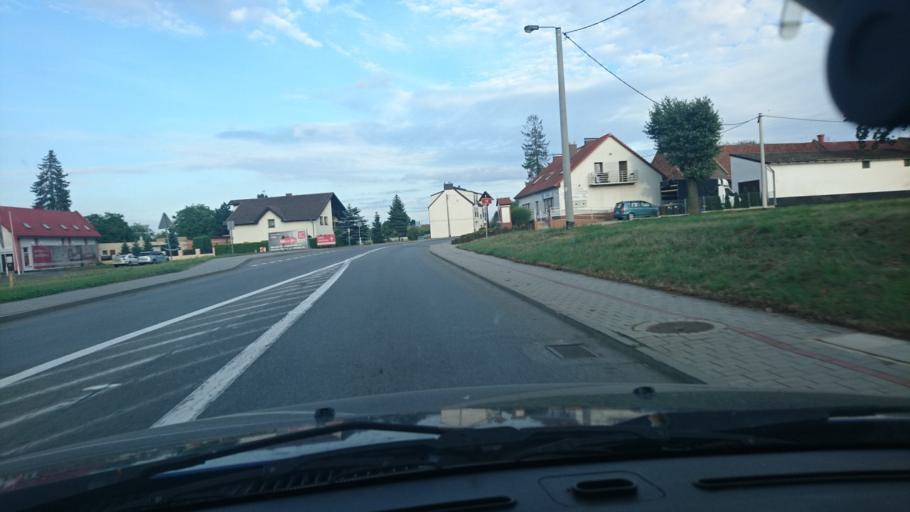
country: PL
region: Opole Voivodeship
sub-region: Powiat oleski
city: Olesno
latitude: 50.8738
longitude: 18.4261
